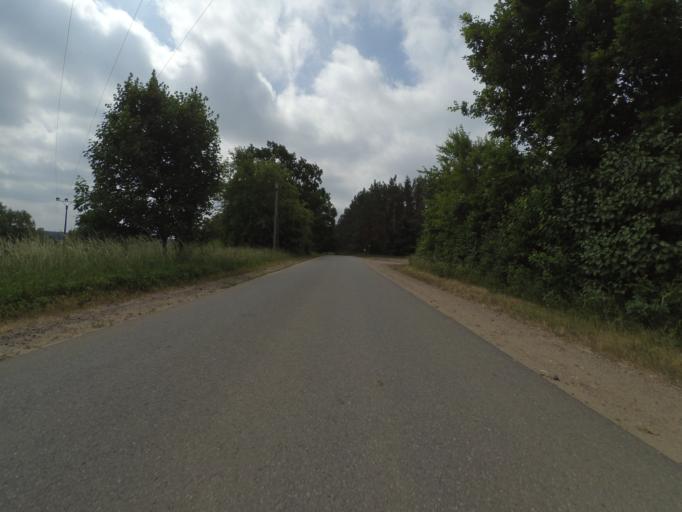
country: DE
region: Mecklenburg-Vorpommern
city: Krakow am See
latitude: 53.6001
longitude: 12.3840
